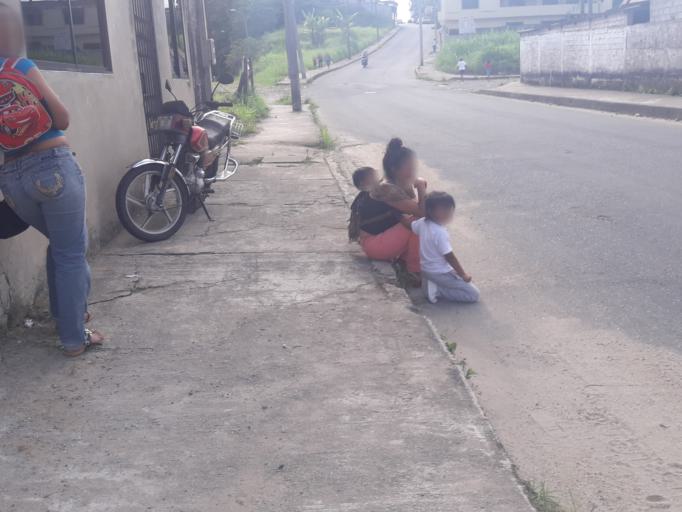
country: EC
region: Napo
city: Tena
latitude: -0.9897
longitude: -77.8113
